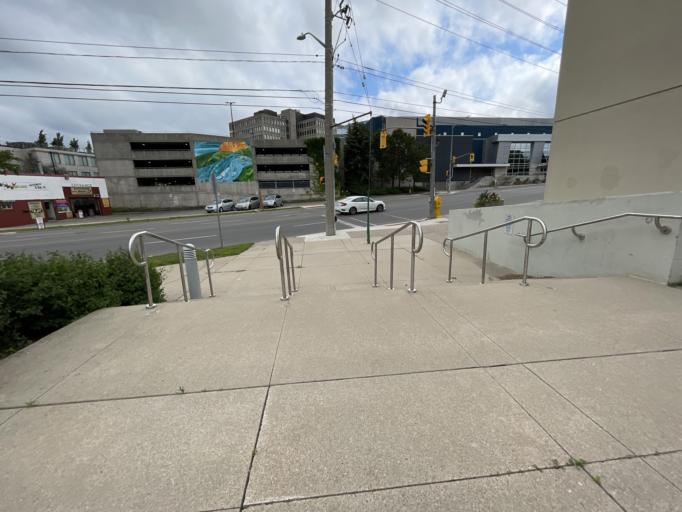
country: CA
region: Ontario
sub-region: Wellington County
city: Guelph
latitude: 43.5475
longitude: -80.2458
